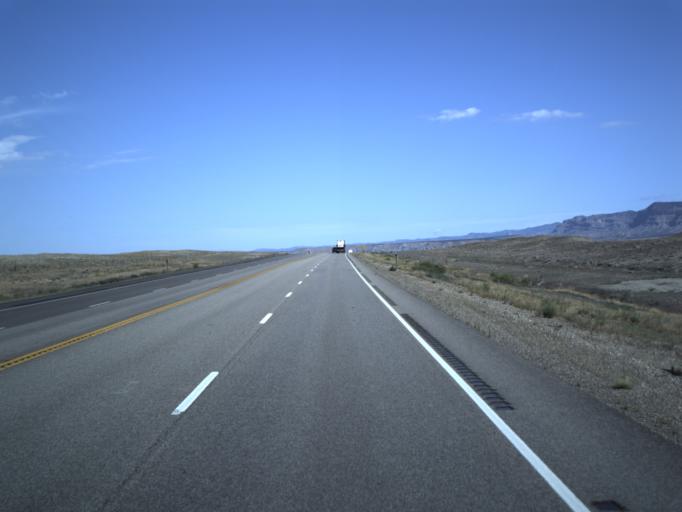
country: US
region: Utah
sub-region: Carbon County
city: East Carbon City
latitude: 39.2997
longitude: -110.3564
